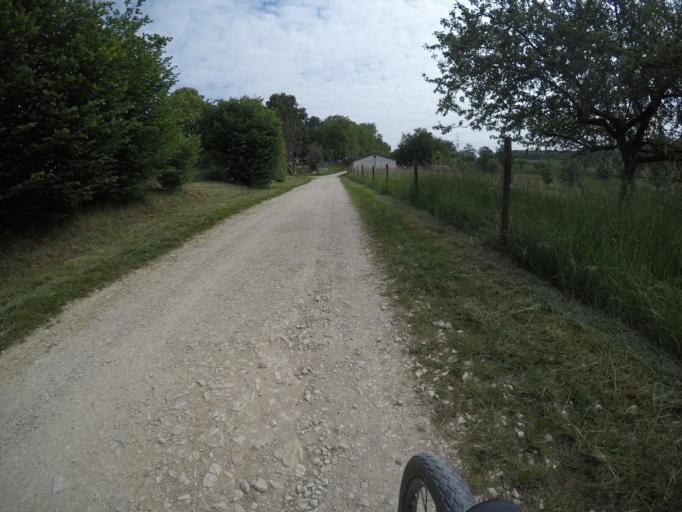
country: DE
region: Baden-Wuerttemberg
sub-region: Regierungsbezirk Stuttgart
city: Oberboihingen
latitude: 48.6491
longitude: 9.3862
